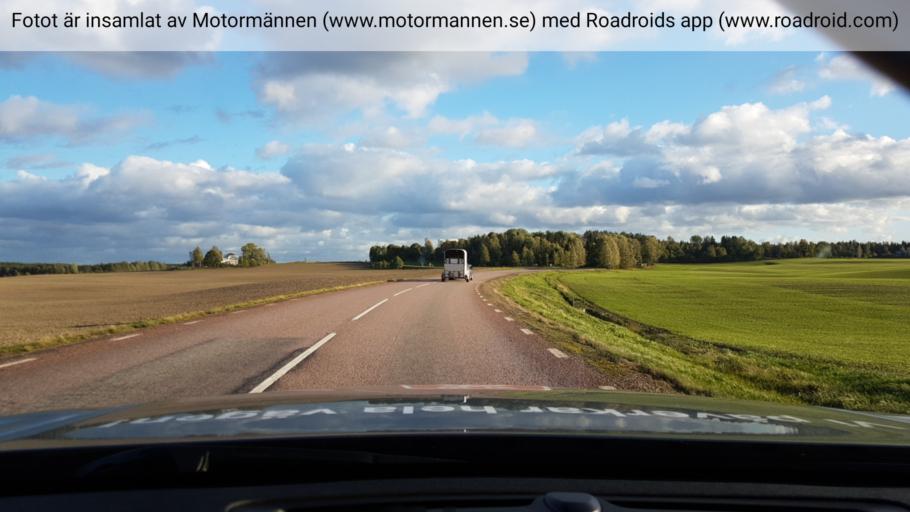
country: SE
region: Vaermland
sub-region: Karlstads Kommun
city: Molkom
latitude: 59.5636
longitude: 13.7726
